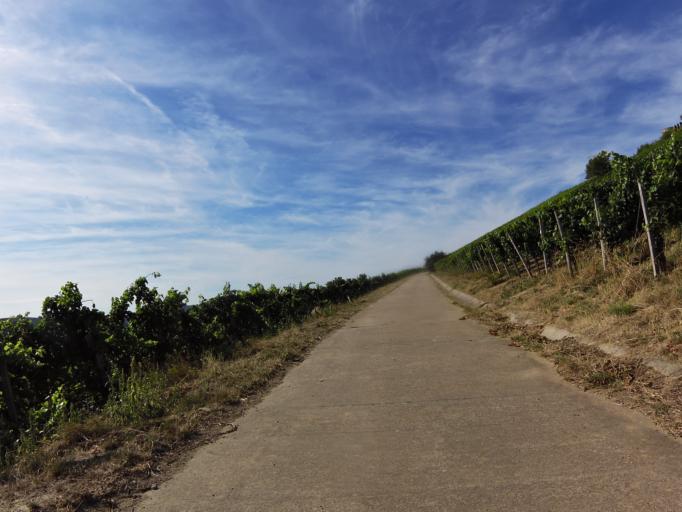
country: DE
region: Bavaria
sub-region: Regierungsbezirk Unterfranken
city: Randersacker
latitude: 49.7480
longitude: 9.9927
